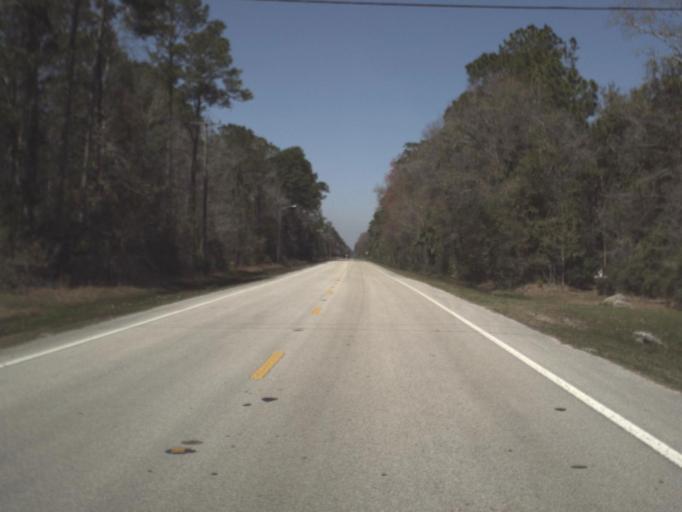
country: US
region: Florida
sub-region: Leon County
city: Woodville
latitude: 30.1709
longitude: -84.2089
